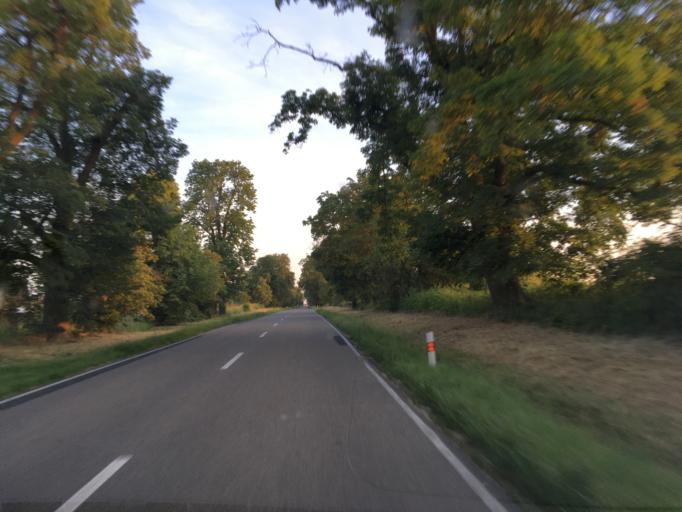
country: CZ
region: South Moravian
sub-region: Okres Breclav
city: Hlohovec
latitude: 48.7568
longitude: 16.7690
